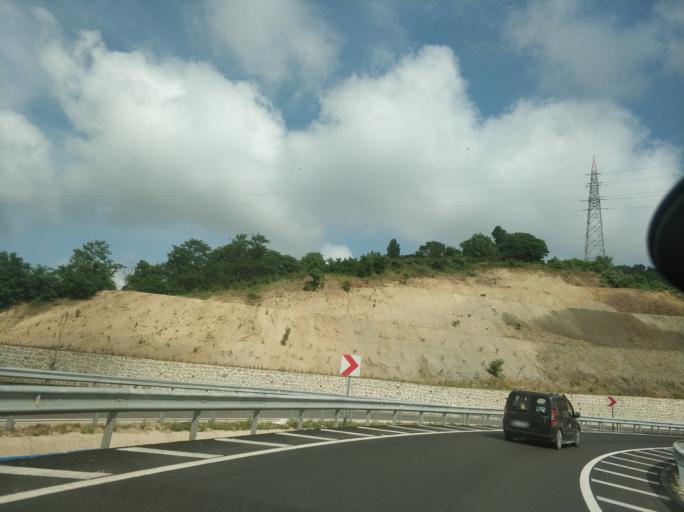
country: TR
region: Ordu
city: Ordu
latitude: 40.9536
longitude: 37.9040
